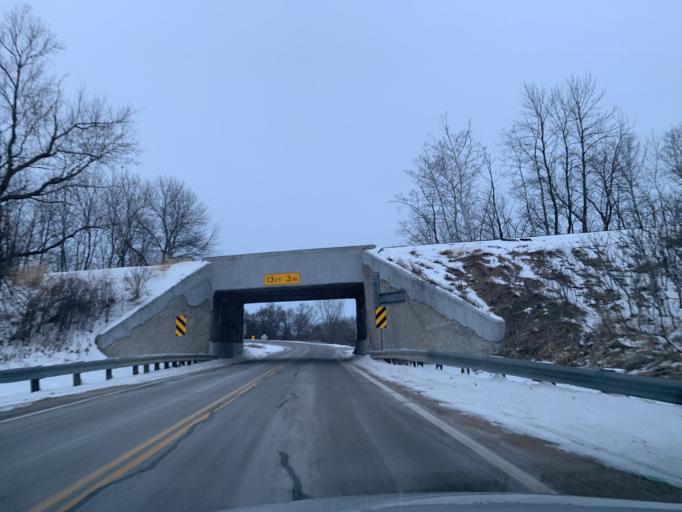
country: US
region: Minnesota
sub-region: Carver County
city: Cologne
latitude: 44.7757
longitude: -93.7558
